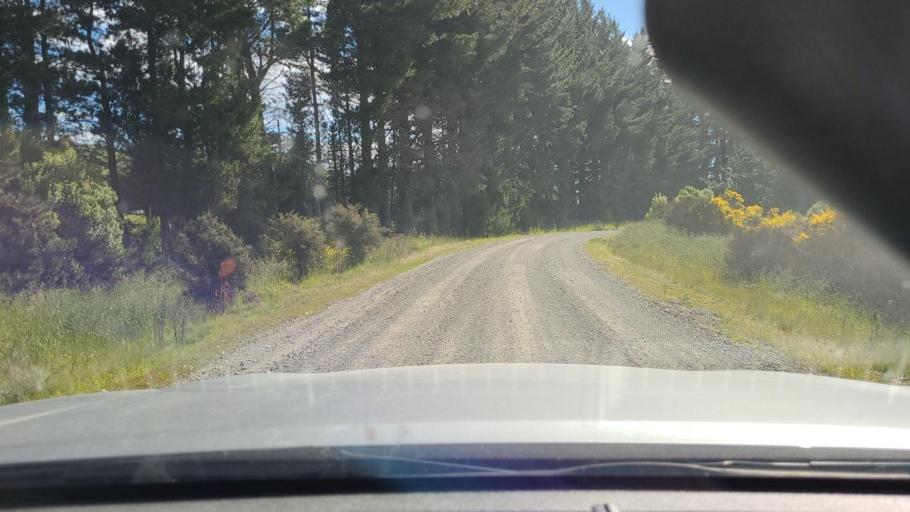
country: NZ
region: Southland
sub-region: Southland District
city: Te Anau
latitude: -45.6965
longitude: 167.6551
